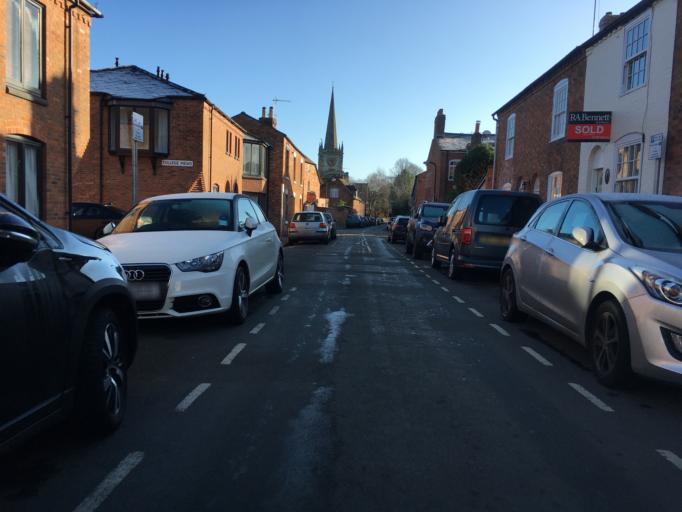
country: GB
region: England
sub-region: Warwickshire
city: Stratford-upon-Avon
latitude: 52.1870
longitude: -1.7104
